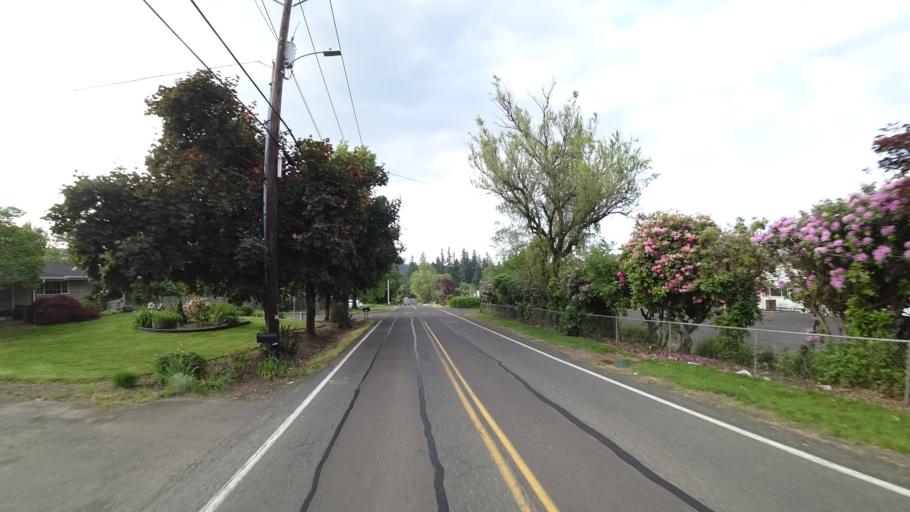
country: US
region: Oregon
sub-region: Clackamas County
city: Happy Valley
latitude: 45.4653
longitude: -122.4968
